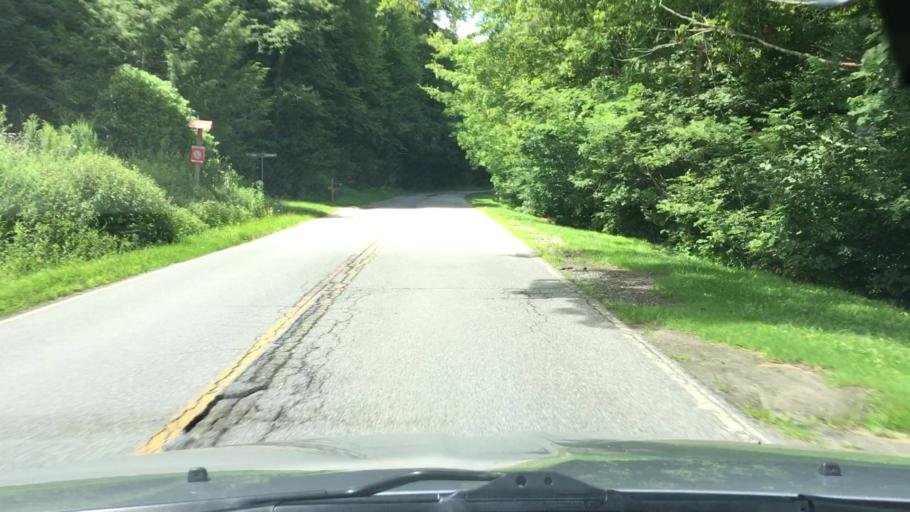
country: US
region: North Carolina
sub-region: Madison County
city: Mars Hill
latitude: 35.9398
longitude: -82.5283
